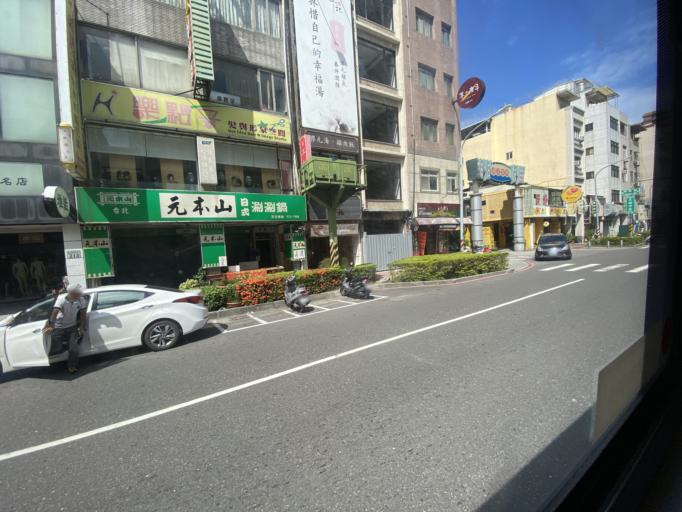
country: TW
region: Kaohsiung
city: Kaohsiung
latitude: 22.6241
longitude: 120.2824
